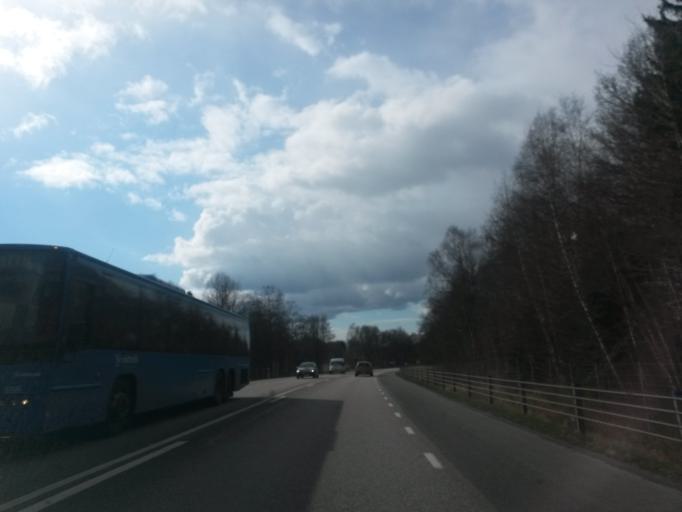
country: SE
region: Vaestra Goetaland
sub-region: Skara Kommun
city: Axvall
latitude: 58.3797
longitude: 13.6884
